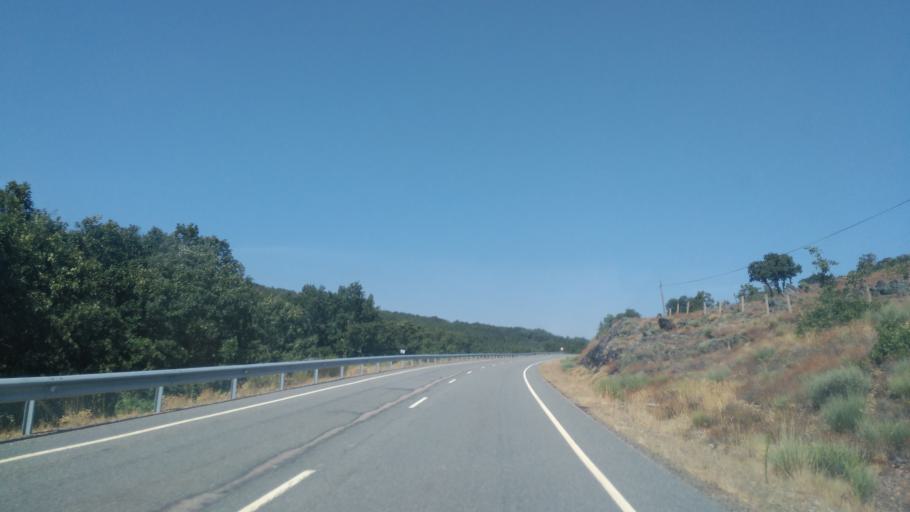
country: ES
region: Castille and Leon
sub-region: Provincia de Salamanca
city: Cereceda de la Sierra
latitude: 40.5856
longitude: -6.0860
